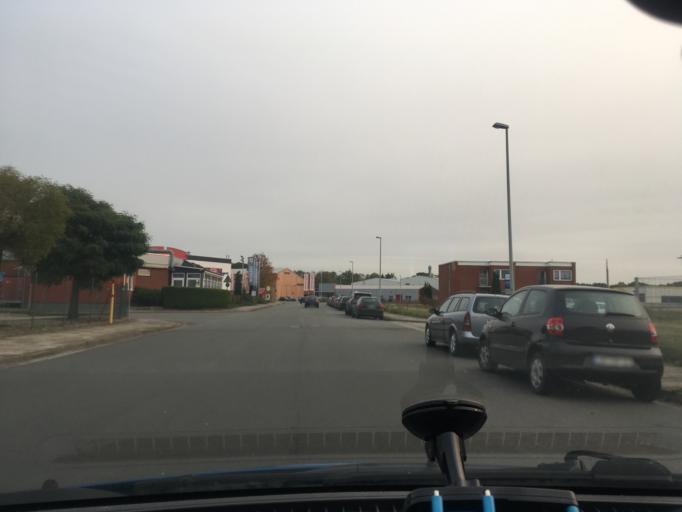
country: DE
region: Lower Saxony
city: Adendorf
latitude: 53.2735
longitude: 10.4237
